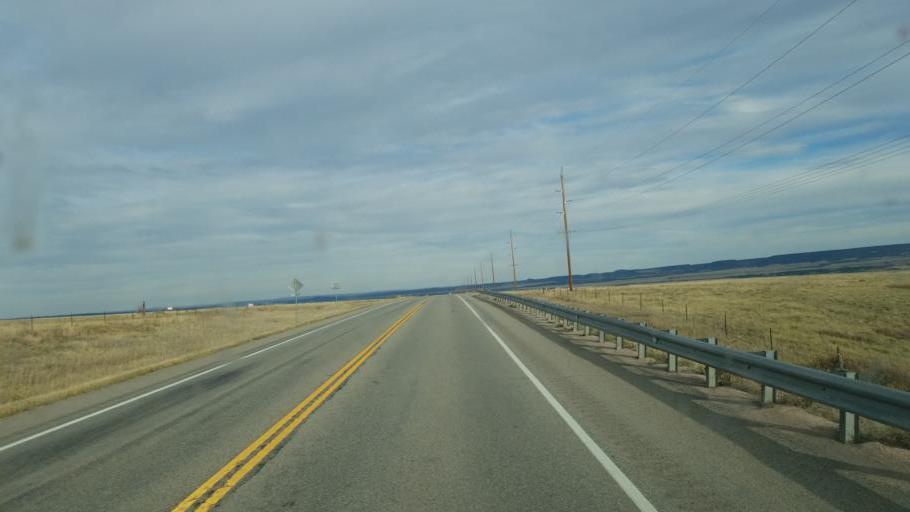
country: US
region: Colorado
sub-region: Huerfano County
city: Walsenburg
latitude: 37.5416
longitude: -105.0571
